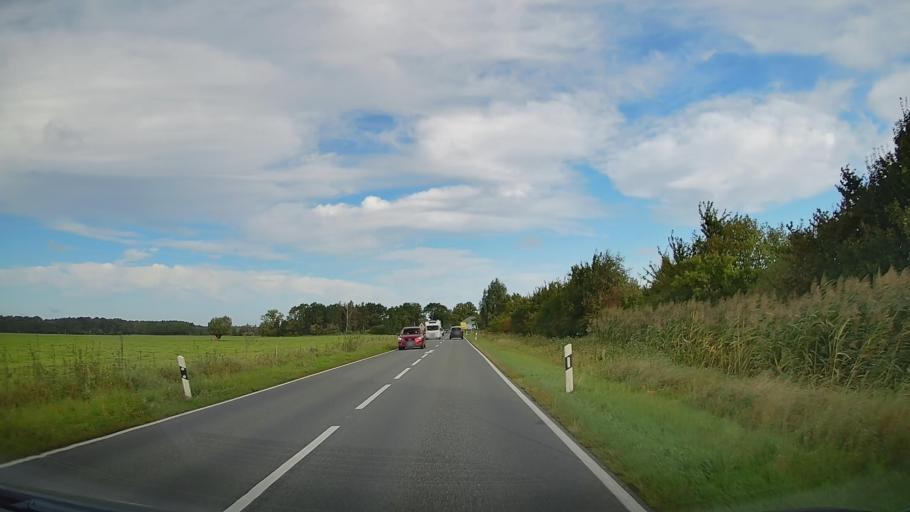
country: DE
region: Mecklenburg-Vorpommern
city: Ostseebad Dierhagen
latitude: 54.2566
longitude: 12.3560
